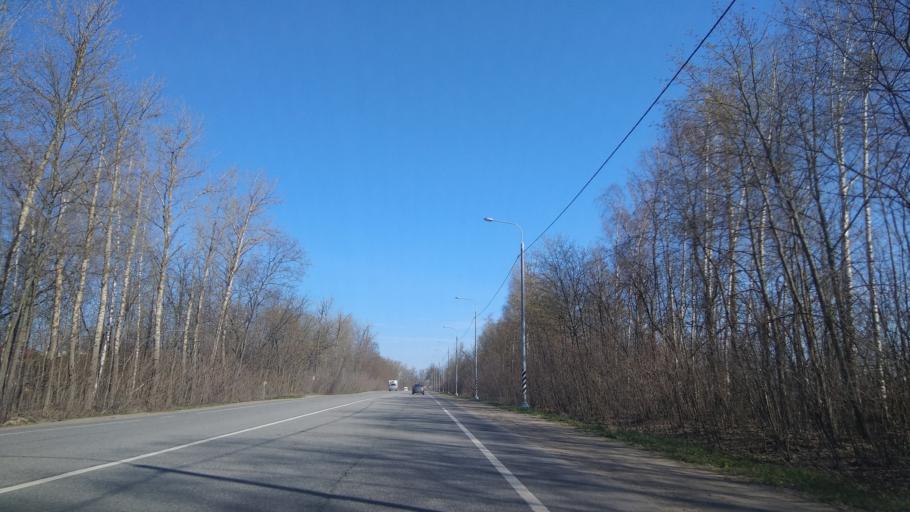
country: RU
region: Moskovskaya
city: Pushkino
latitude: 56.0368
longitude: 37.8705
